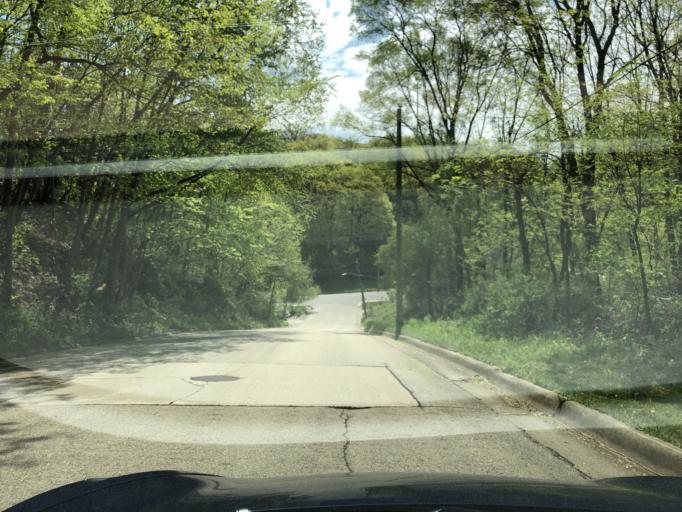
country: US
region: Iowa
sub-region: Dubuque County
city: Dubuque
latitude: 42.4827
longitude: -90.6695
